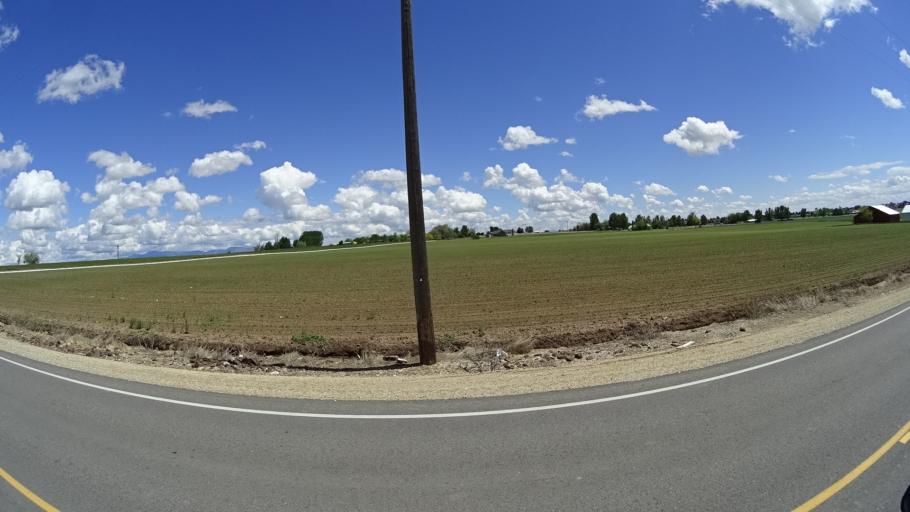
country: US
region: Idaho
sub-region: Ada County
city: Meridian
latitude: 43.5661
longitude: -116.4538
